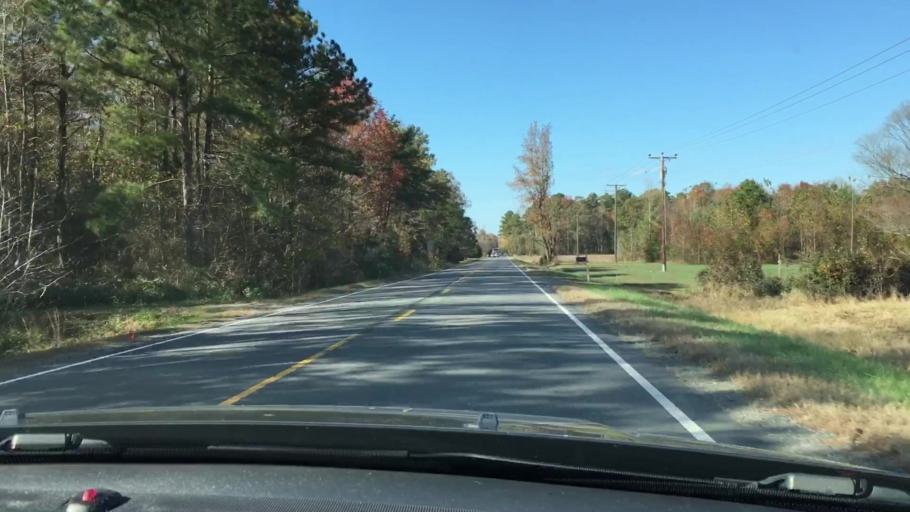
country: US
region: Virginia
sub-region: King William County
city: King William
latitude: 37.6616
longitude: -76.9604
